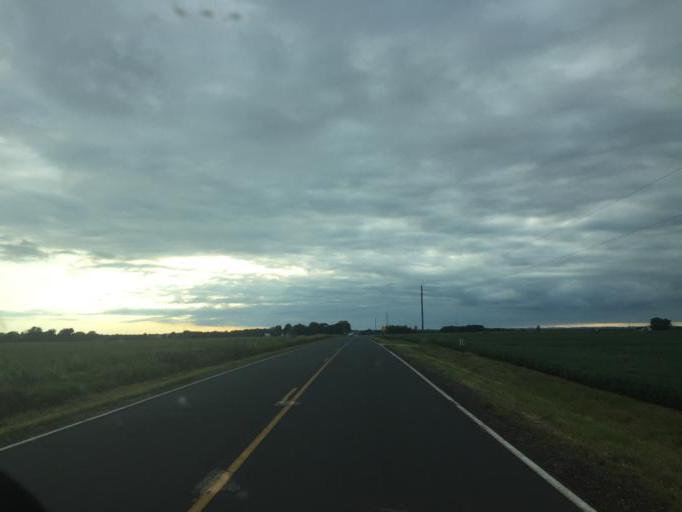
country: US
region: Minnesota
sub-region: Olmsted County
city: Rochester
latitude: 43.9640
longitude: -92.5135
